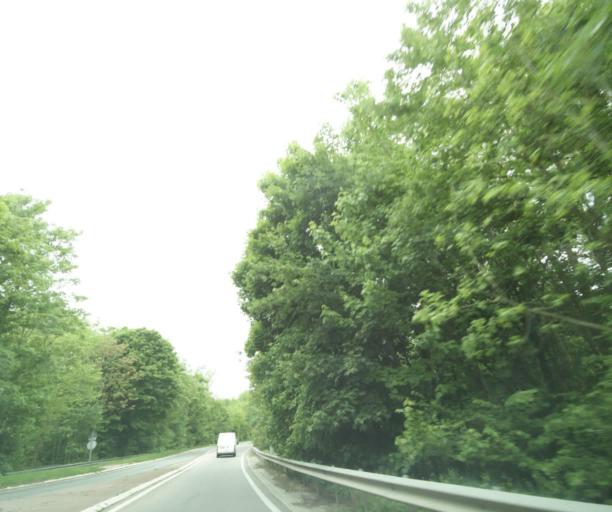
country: FR
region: Ile-de-France
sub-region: Departement des Yvelines
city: Flins-sur-Seine
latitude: 48.9600
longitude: 1.8701
